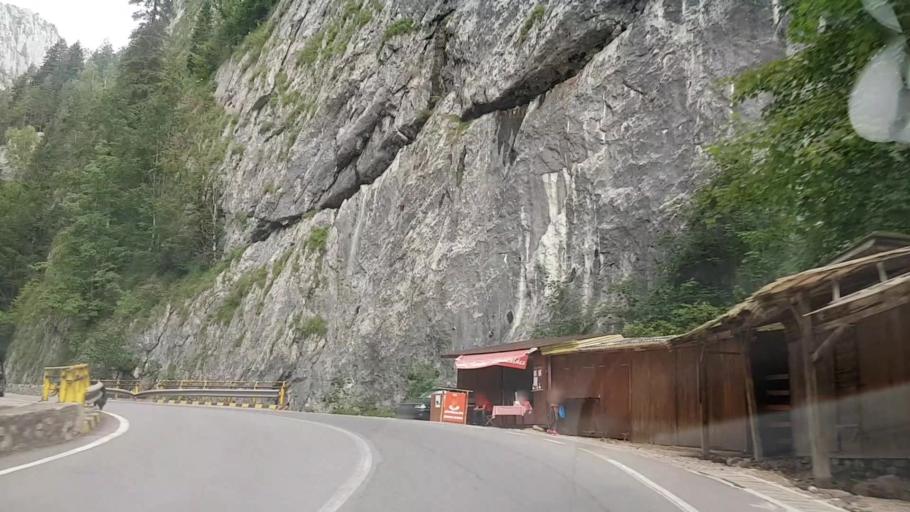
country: RO
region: Neamt
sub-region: Comuna Bicaz Chei
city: Bicaz Chei
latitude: 46.8115
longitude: 25.8245
